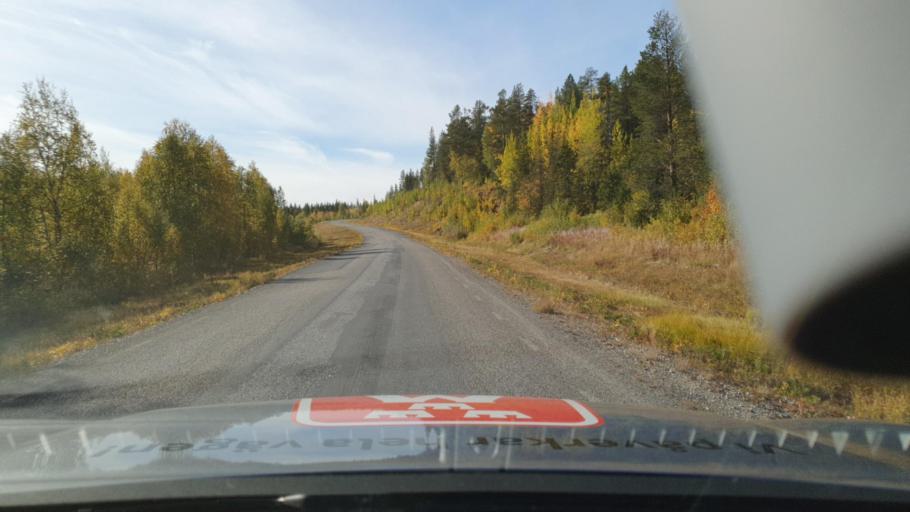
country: SE
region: Norrbotten
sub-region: Jokkmokks Kommun
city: Jokkmokk
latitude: 66.1899
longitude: 20.0307
